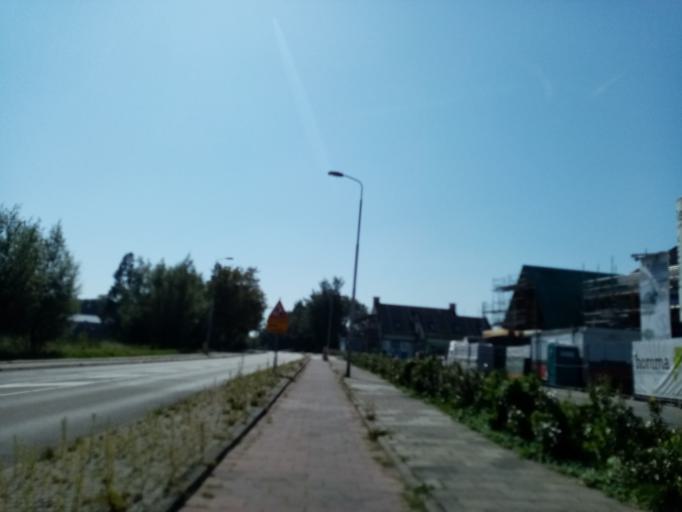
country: NL
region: South Holland
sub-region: Gemeente Lisse
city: Lisse
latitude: 52.2553
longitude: 4.5585
